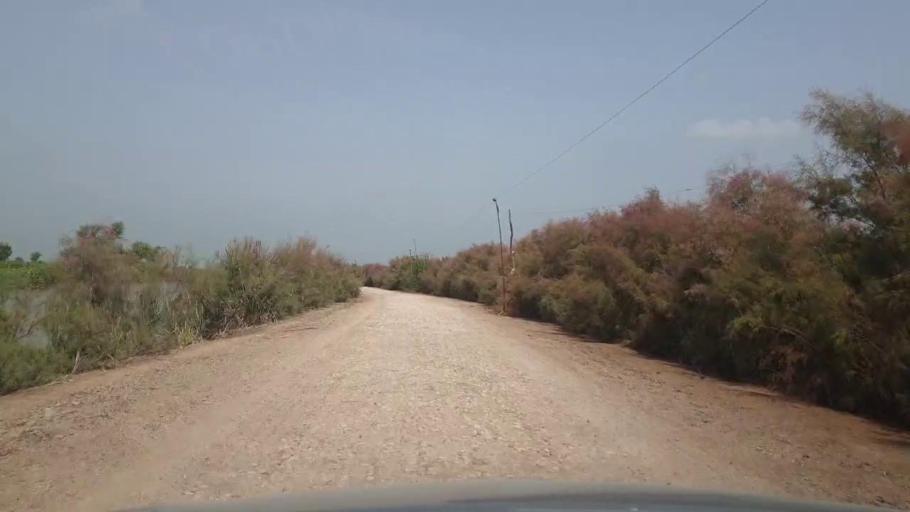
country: PK
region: Sindh
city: Garhi Yasin
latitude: 27.9559
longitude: 68.3648
